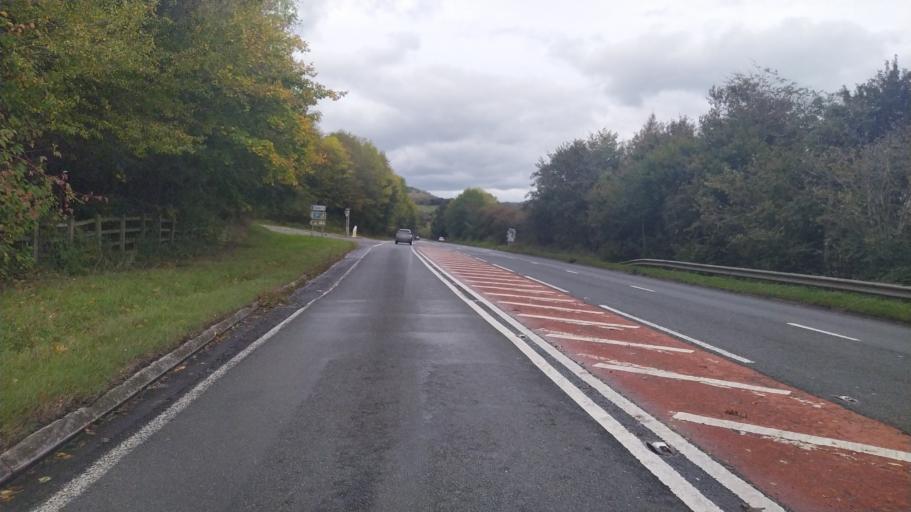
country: GB
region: England
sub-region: Dorset
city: Bridport
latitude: 50.7272
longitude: -2.7776
